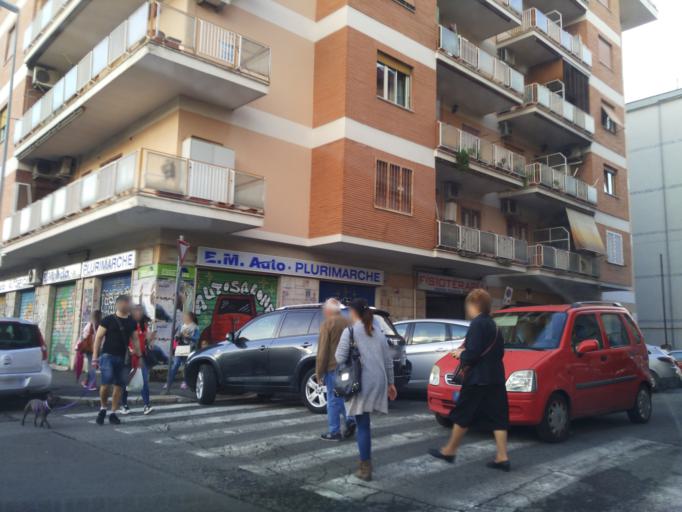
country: IT
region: Latium
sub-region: Citta metropolitana di Roma Capitale
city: Rome
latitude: 41.8828
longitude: 12.5610
